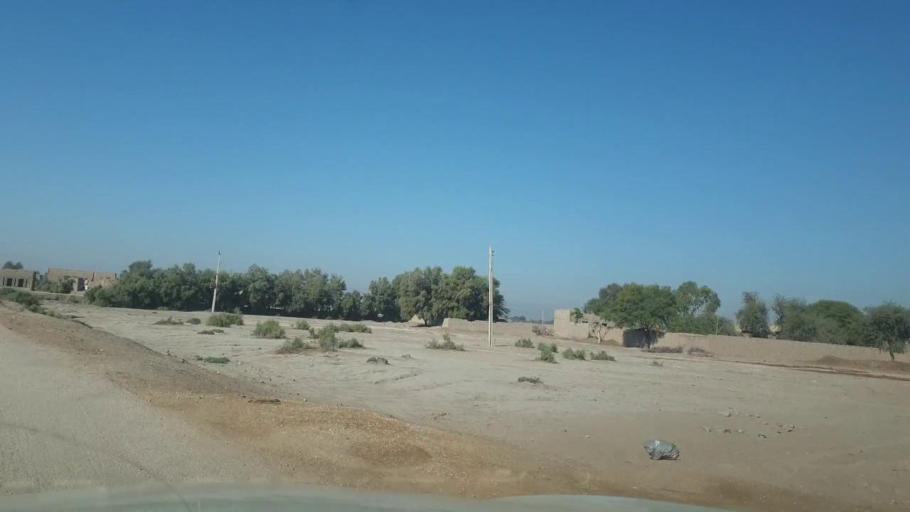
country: PK
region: Sindh
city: Bhan
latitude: 26.5482
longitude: 67.6559
